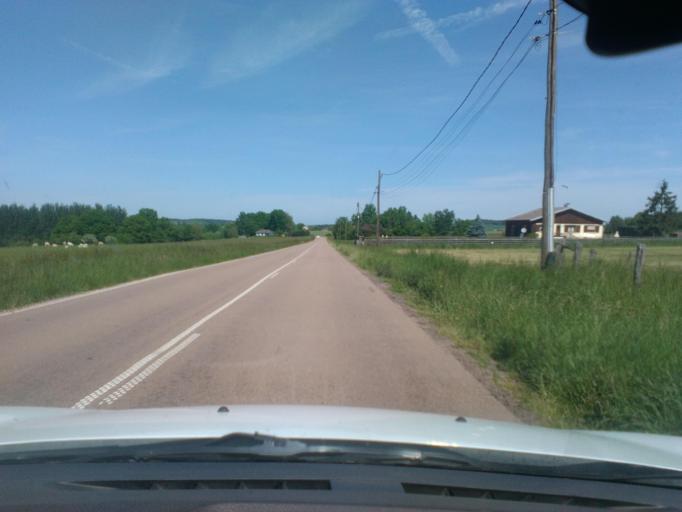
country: FR
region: Lorraine
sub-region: Departement des Vosges
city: Rambervillers
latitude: 48.3709
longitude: 6.6147
